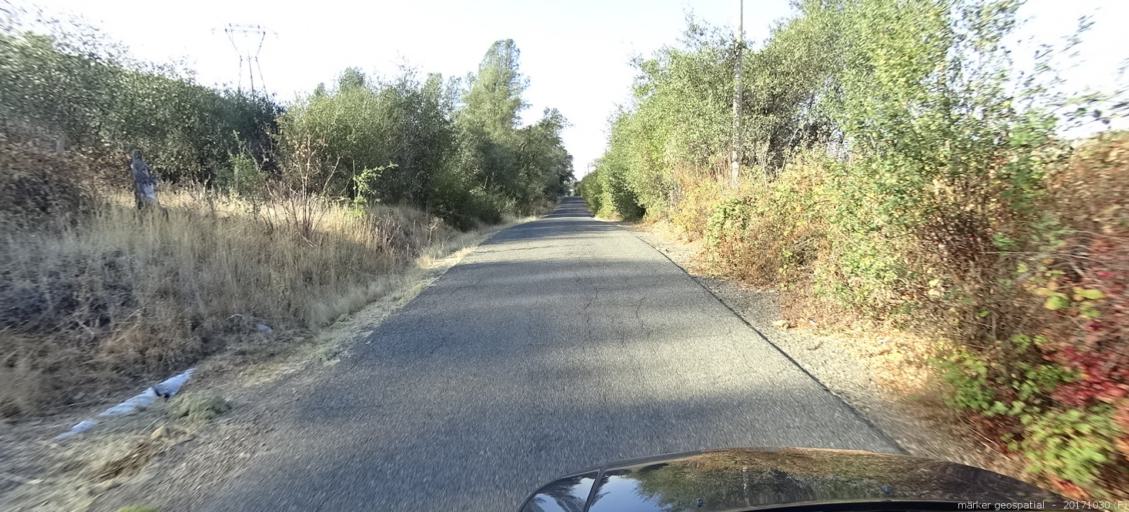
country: US
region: California
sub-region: Shasta County
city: Palo Cedro
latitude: 40.5647
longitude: -122.1509
